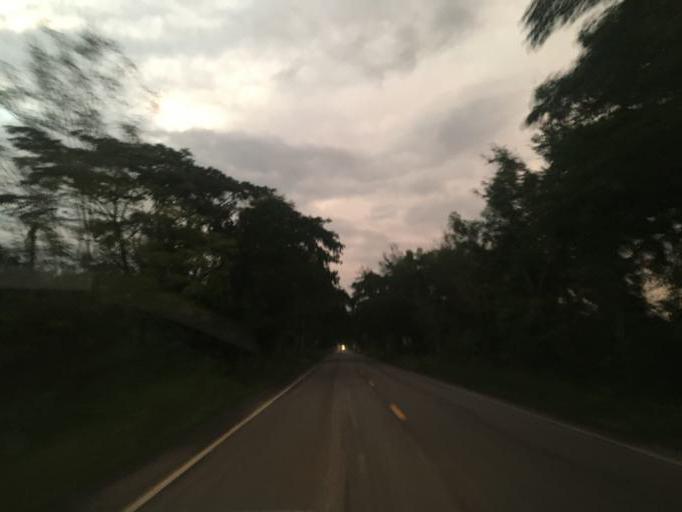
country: TH
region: Changwat Udon Thani
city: Udon Thani
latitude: 17.3556
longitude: 102.7202
